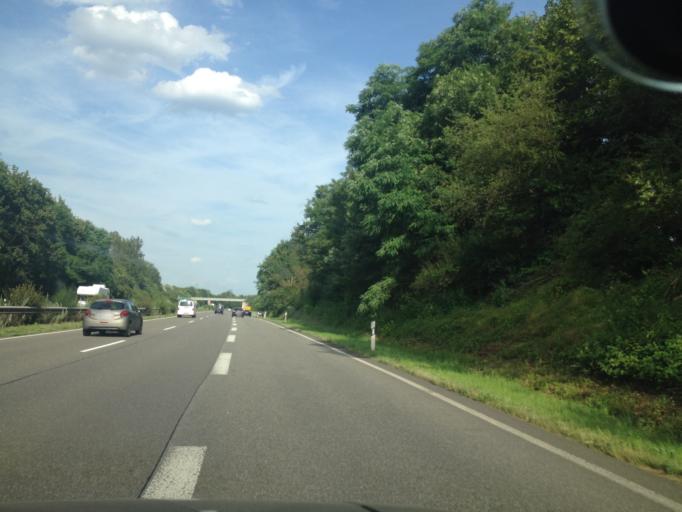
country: DE
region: Rheinland-Pfalz
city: Lingenfeld
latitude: 49.2363
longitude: 8.3433
